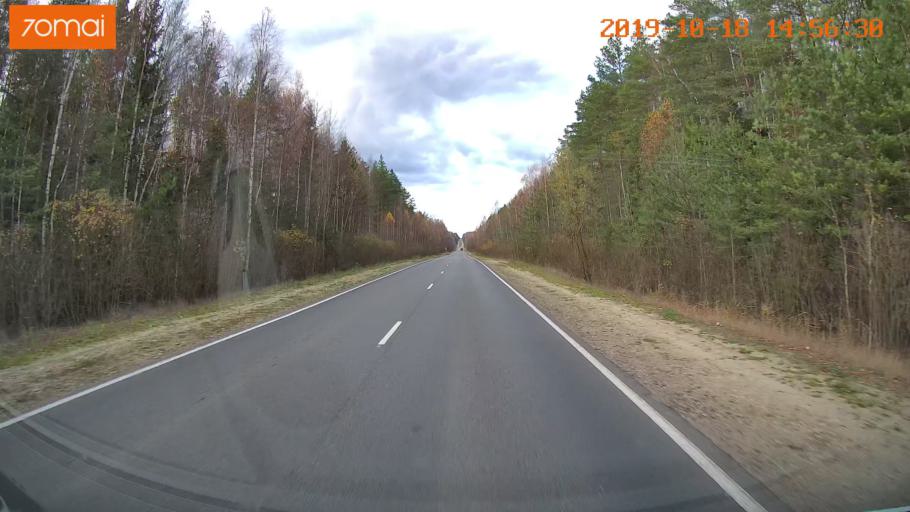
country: RU
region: Vladimir
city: Kurlovo
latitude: 55.4655
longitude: 40.5871
